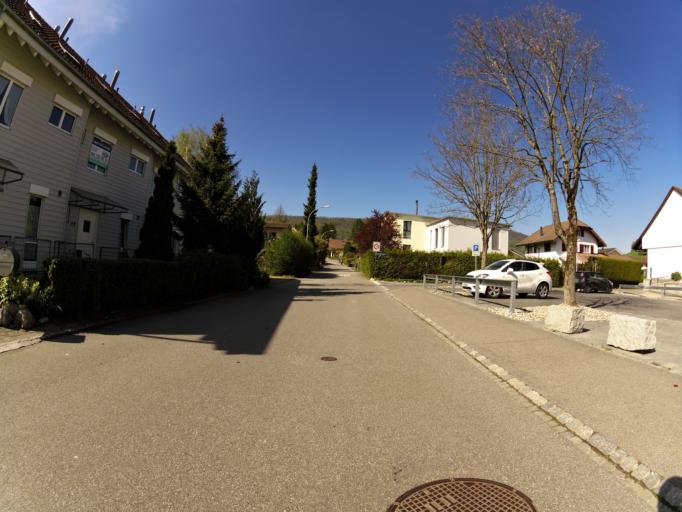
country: CH
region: Solothurn
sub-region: Bezirk Goesgen
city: Niedererlinsbach
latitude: 47.3985
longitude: 8.0061
